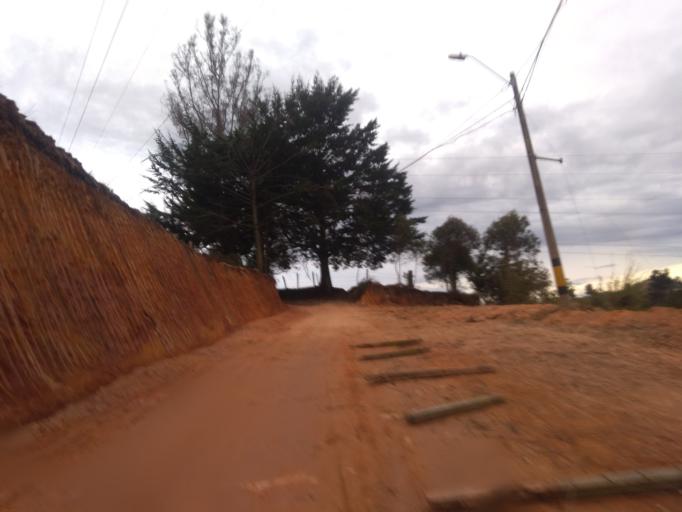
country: CO
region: Antioquia
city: Bello
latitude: 6.3550
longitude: -75.6098
